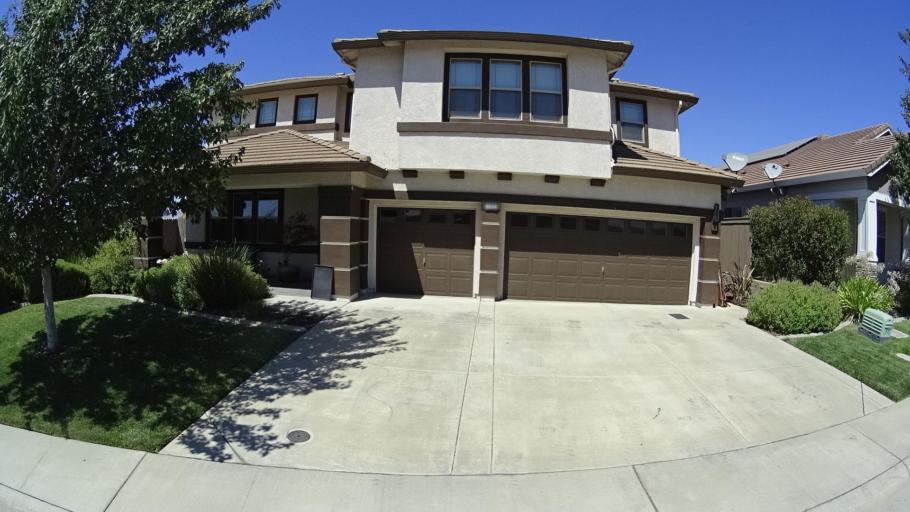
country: US
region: California
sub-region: Placer County
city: Rocklin
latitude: 38.8225
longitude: -121.2882
